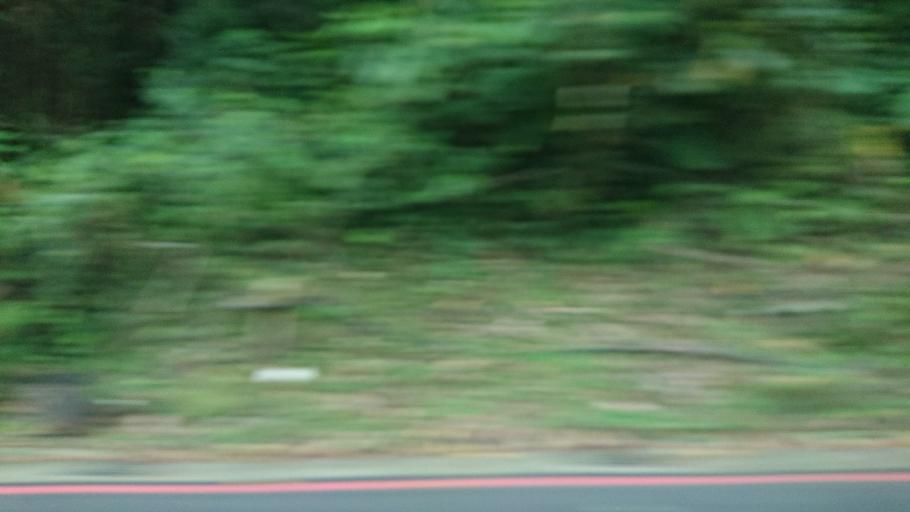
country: TW
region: Taiwan
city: Daxi
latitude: 24.8734
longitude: 121.3870
